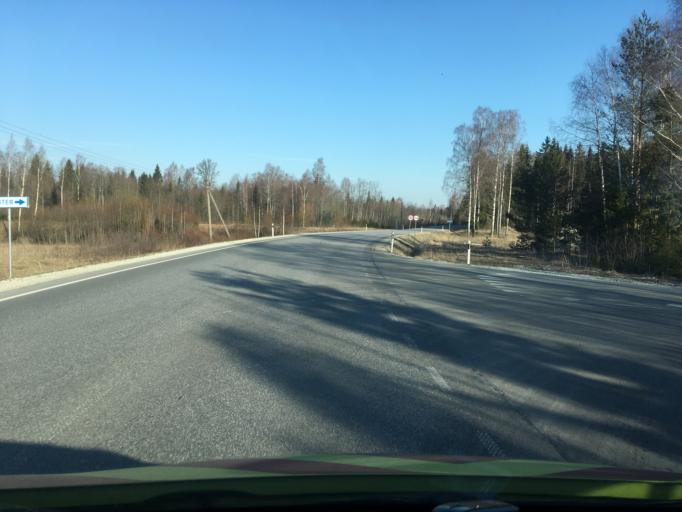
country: EE
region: Raplamaa
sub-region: Rapla vald
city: Rapla
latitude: 59.0097
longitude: 24.8386
